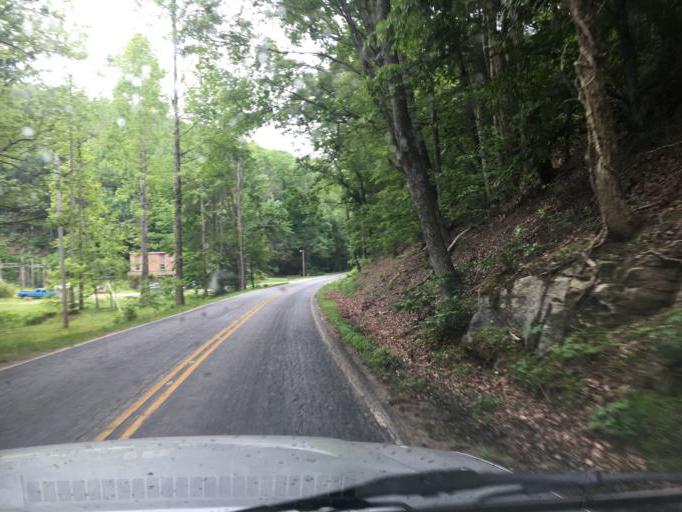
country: US
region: South Carolina
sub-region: Greenville County
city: Tigerville
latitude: 35.1284
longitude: -82.3803
